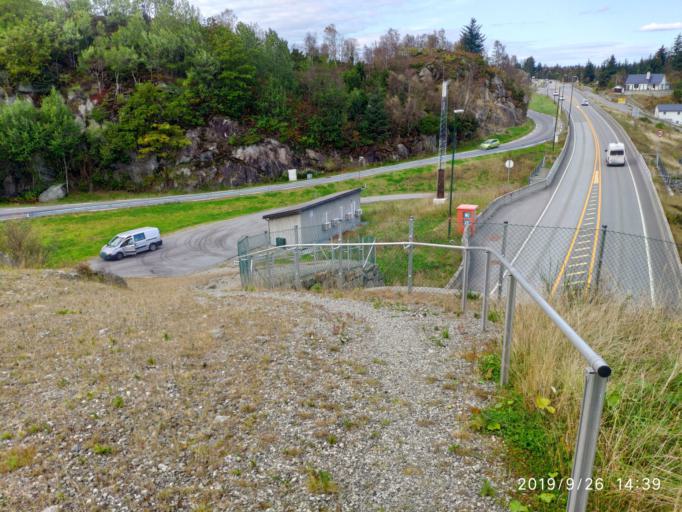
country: NO
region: Rogaland
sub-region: Karmoy
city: Vormedal
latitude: 59.3237
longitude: 5.3715
